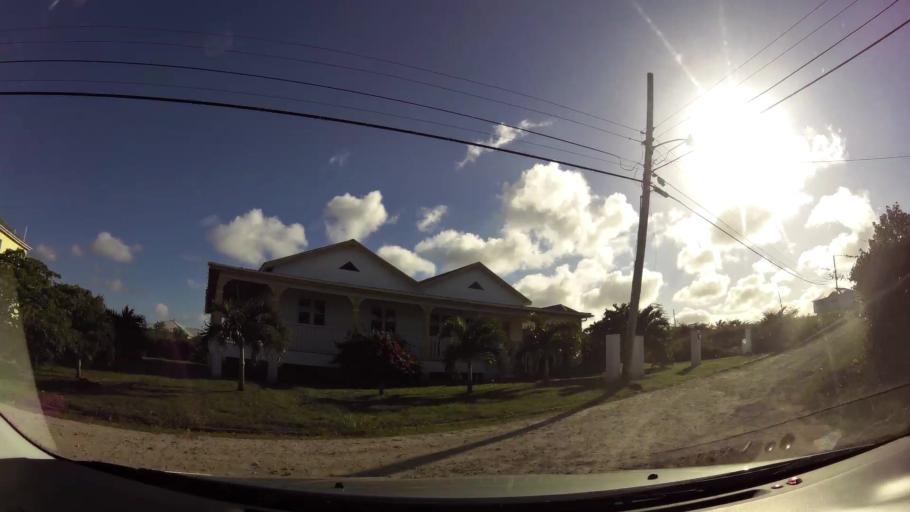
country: AG
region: Saint George
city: Piggotts
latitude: 17.0999
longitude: -61.8025
